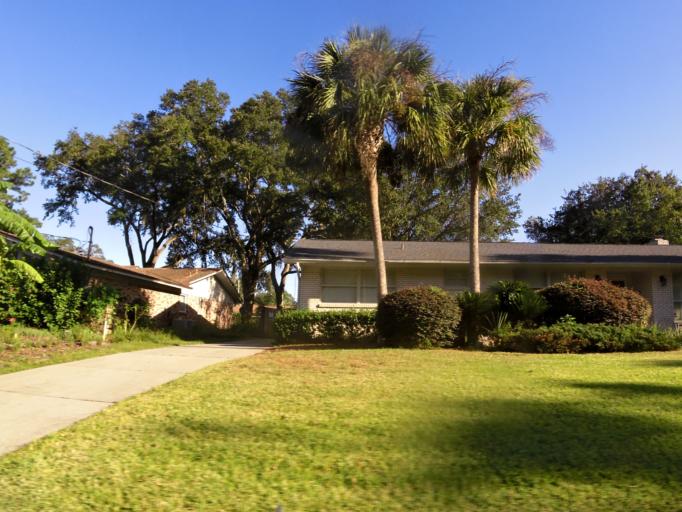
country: US
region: Florida
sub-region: Duval County
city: Jacksonville
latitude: 30.2537
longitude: -81.6362
